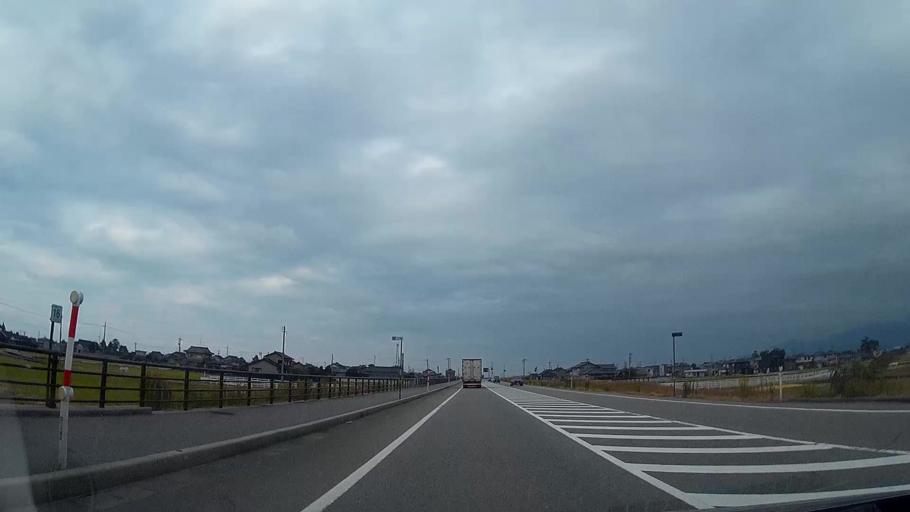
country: JP
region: Toyama
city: Nyuzen
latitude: 36.9187
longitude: 137.4645
